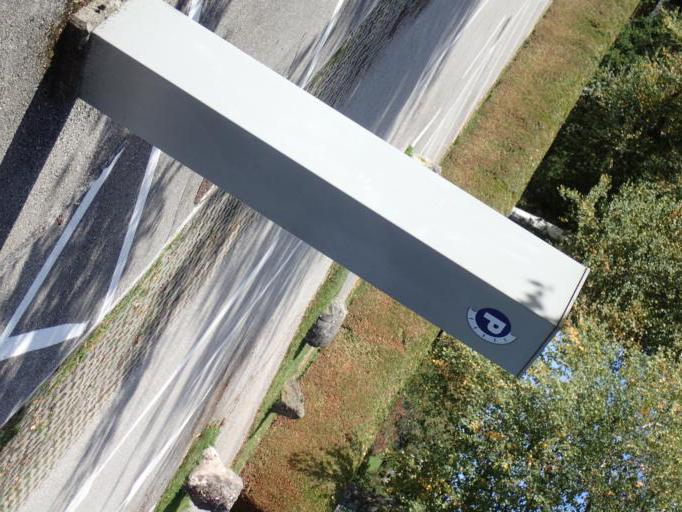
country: AT
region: Salzburg
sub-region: Politischer Bezirk Salzburg-Umgebung
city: Mattsee
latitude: 47.9733
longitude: 13.1063
